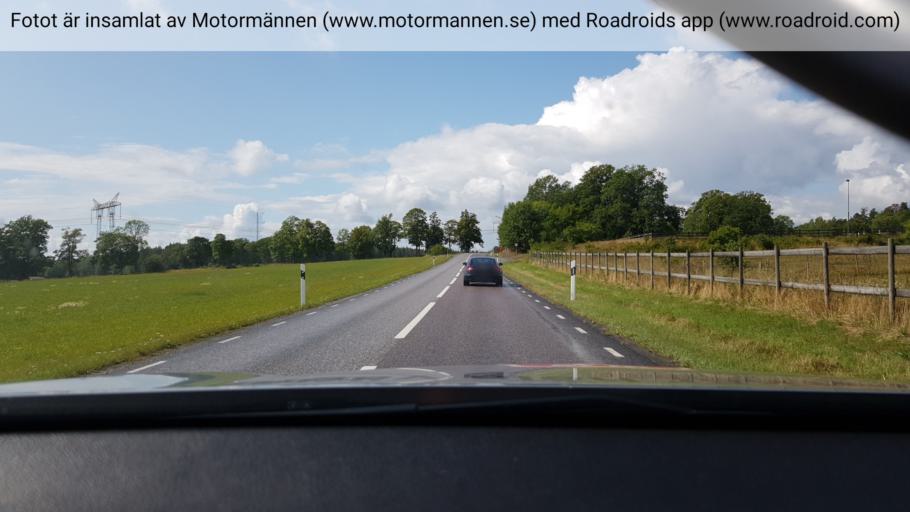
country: SE
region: Stockholm
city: Stenhamra
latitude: 59.2985
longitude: 17.6603
